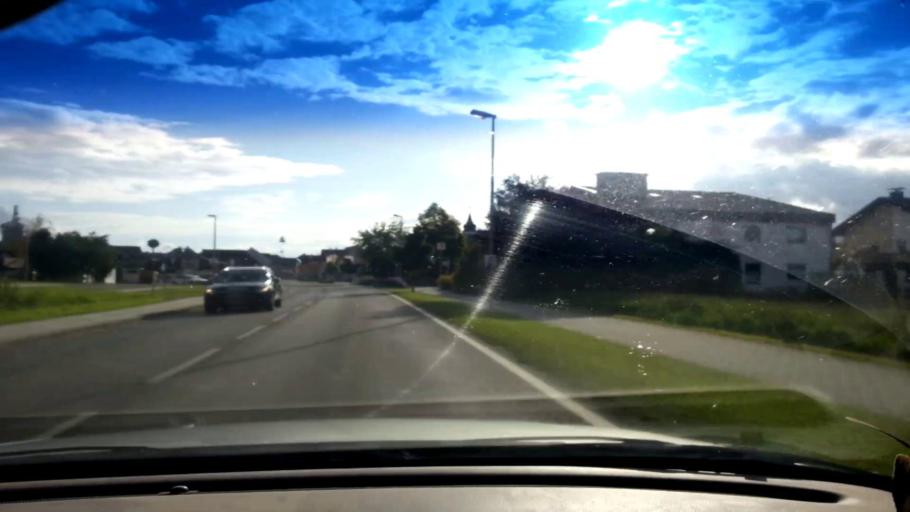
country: DE
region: Bavaria
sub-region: Upper Franconia
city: Ebensfeld
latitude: 50.0687
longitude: 10.9612
